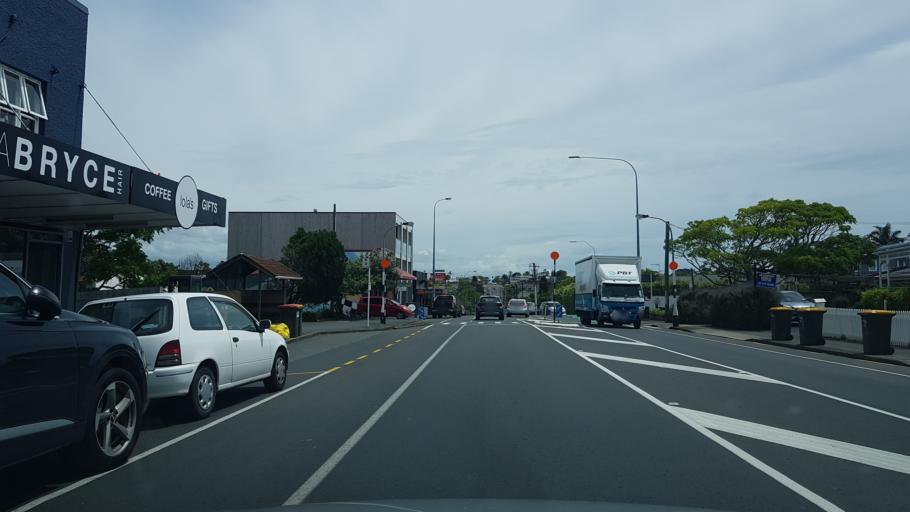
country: NZ
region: Auckland
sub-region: Auckland
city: North Shore
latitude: -36.8134
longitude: 174.7925
